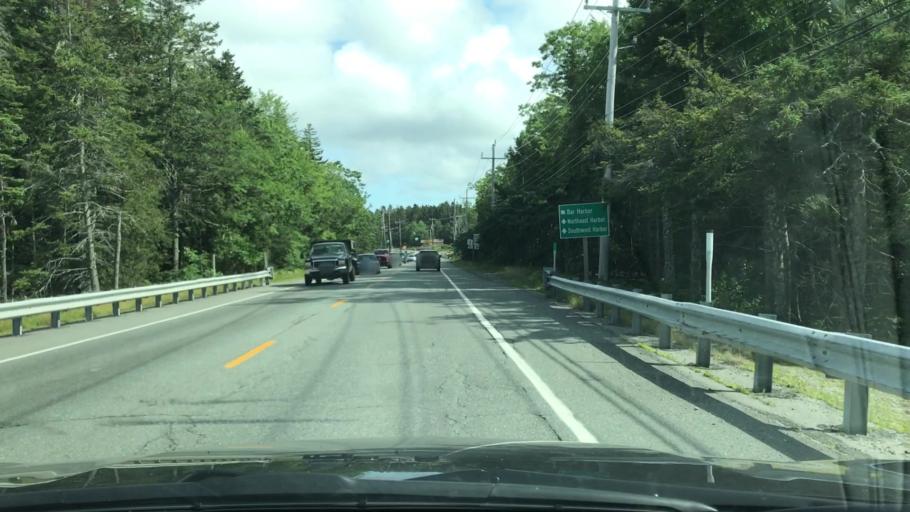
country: US
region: Maine
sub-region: Hancock County
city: Trenton
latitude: 44.4246
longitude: -68.3652
